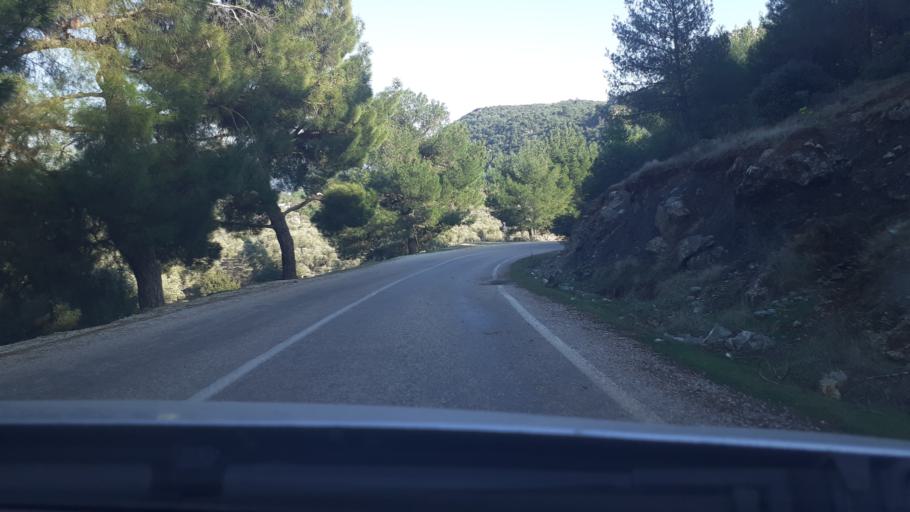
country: TR
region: Hatay
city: Aktepe
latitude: 36.7346
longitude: 36.4681
